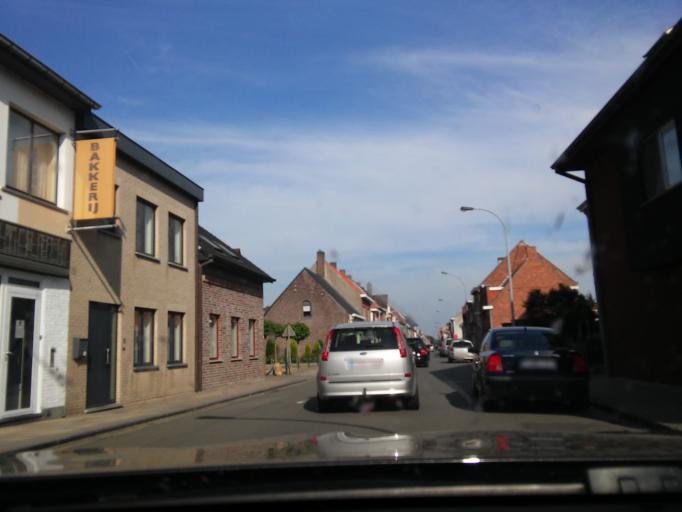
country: BE
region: Flanders
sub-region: Provincie Oost-Vlaanderen
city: Sint-Laureins
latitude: 51.2435
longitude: 3.5183
